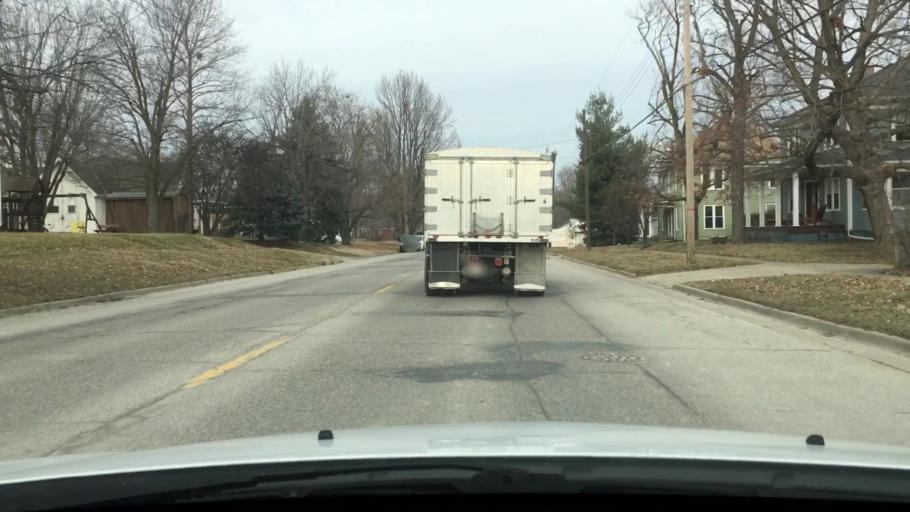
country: US
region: Illinois
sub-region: Pike County
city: Pittsfield
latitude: 39.6104
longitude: -90.8030
